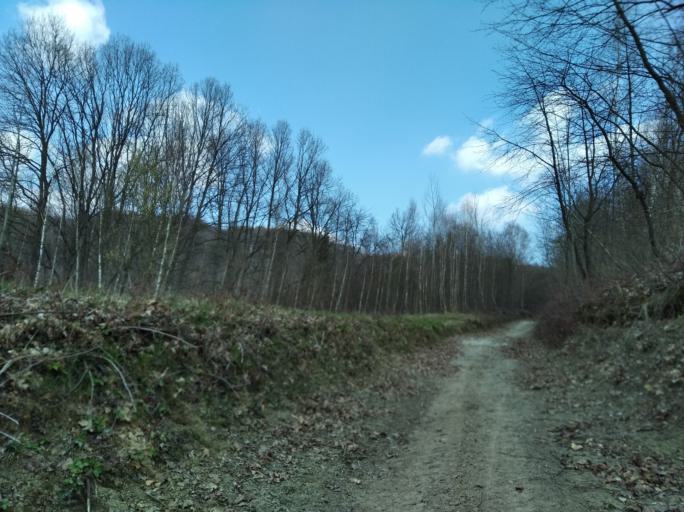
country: PL
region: Subcarpathian Voivodeship
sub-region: Powiat strzyzowski
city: Strzyzow
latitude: 49.8426
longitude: 21.8387
